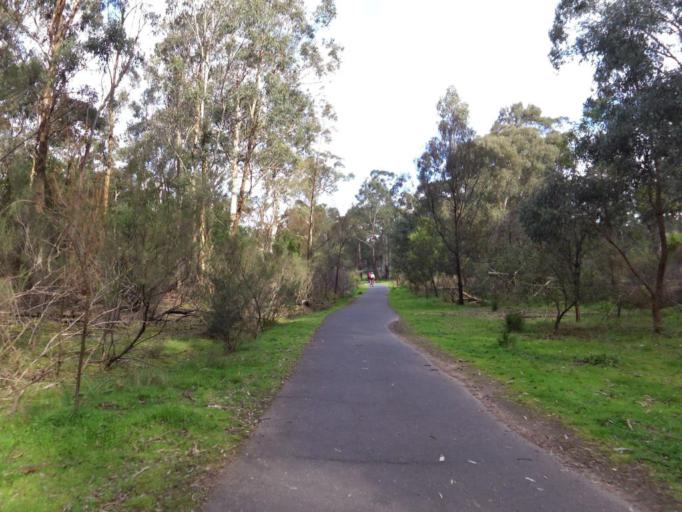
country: AU
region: Victoria
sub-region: Nillumbik
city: Eltham
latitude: -37.7494
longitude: 145.1739
